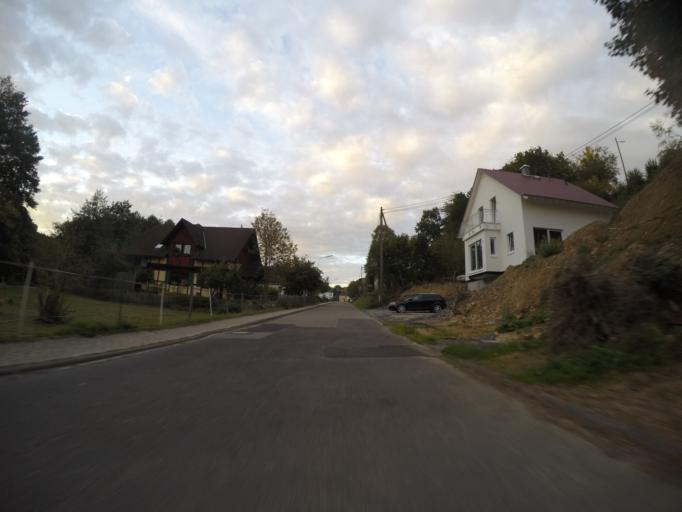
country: DE
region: Rheinland-Pfalz
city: Stebach
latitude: 50.5113
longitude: 7.6614
